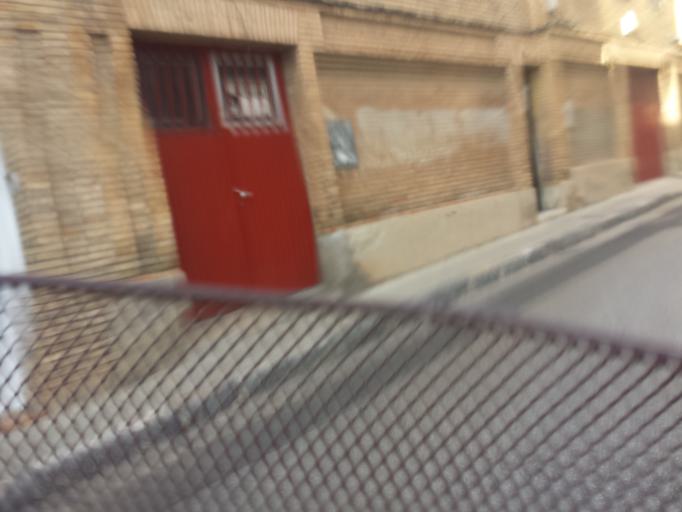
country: ES
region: Aragon
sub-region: Provincia de Zaragoza
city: Delicias
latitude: 41.6318
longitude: -0.8894
